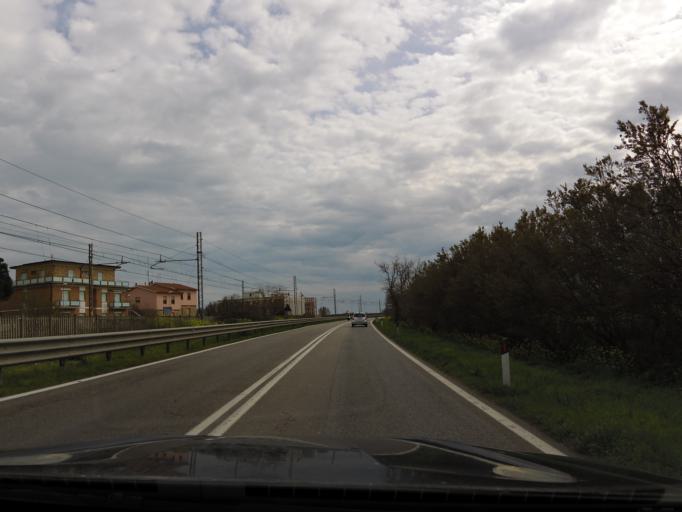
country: IT
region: The Marches
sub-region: Provincia di Macerata
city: Porto Recanati
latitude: 43.4125
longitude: 13.6740
